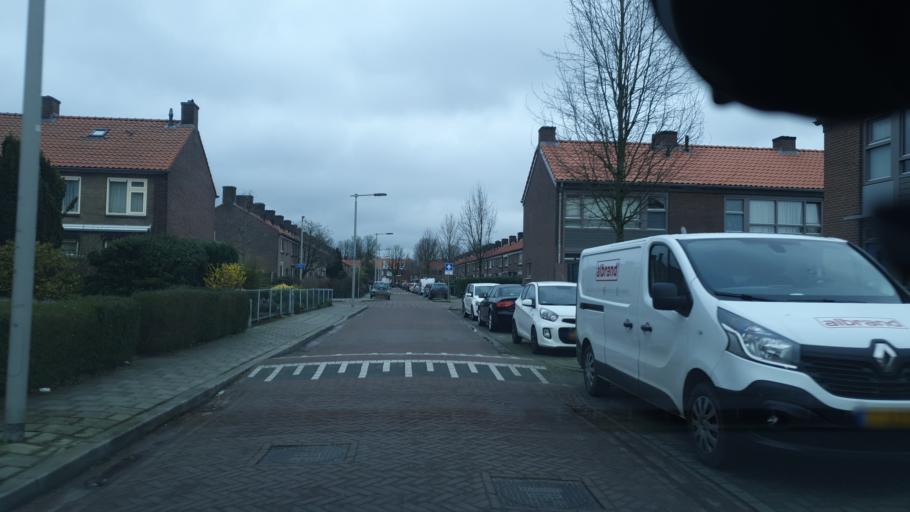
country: NL
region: Gelderland
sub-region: Gemeente Arnhem
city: Arnhem
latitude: 51.9622
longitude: 5.9157
